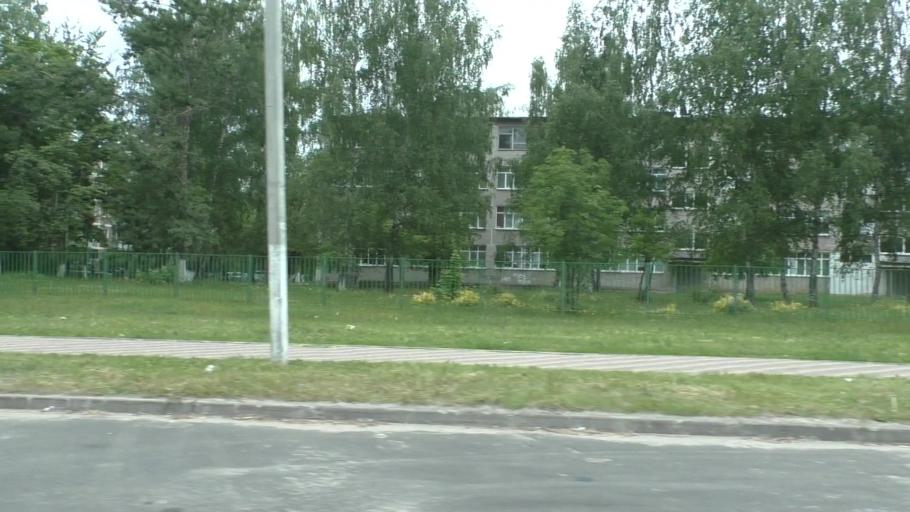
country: RU
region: Moskovskaya
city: Yegor'yevsk
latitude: 55.3663
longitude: 39.0640
